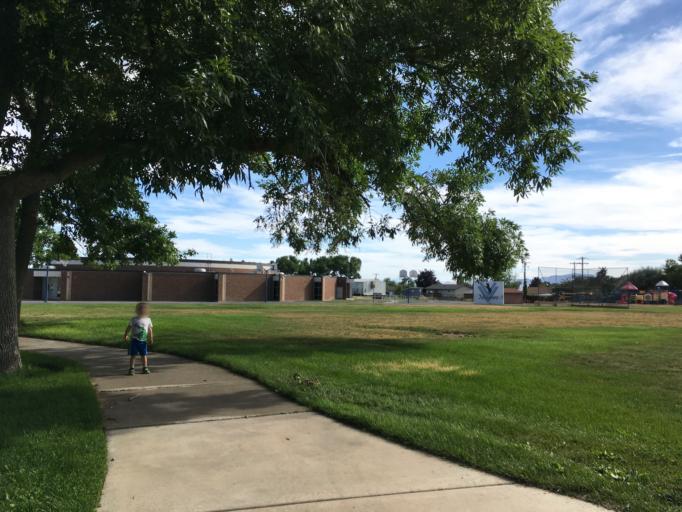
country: US
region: Utah
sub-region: Davis County
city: Hill Air Force Bace
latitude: 41.0845
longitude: -111.9981
